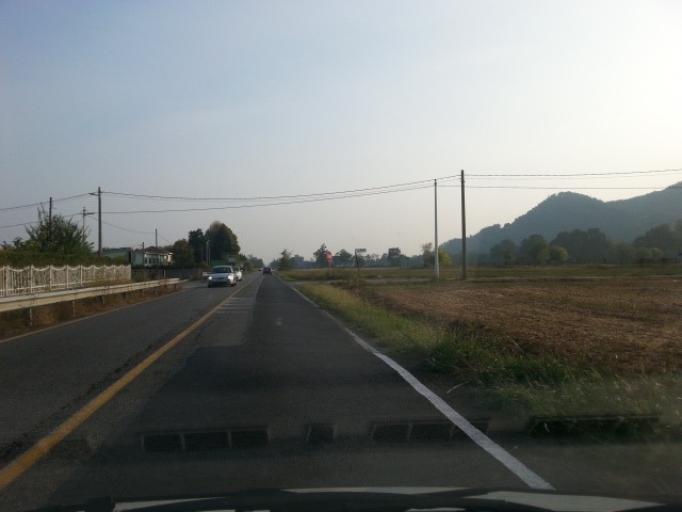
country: IT
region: Piedmont
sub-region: Provincia di Torino
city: Bruino
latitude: 45.0086
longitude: 7.4661
